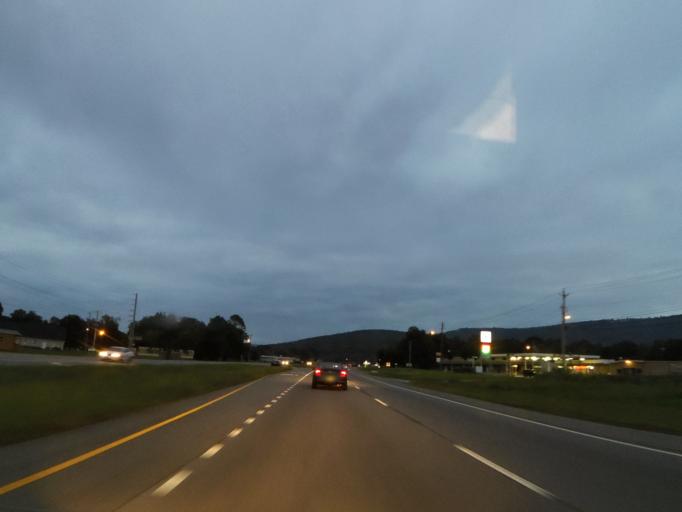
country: US
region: Alabama
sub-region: Madison County
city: Owens Cross Roads
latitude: 34.6982
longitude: -86.3807
